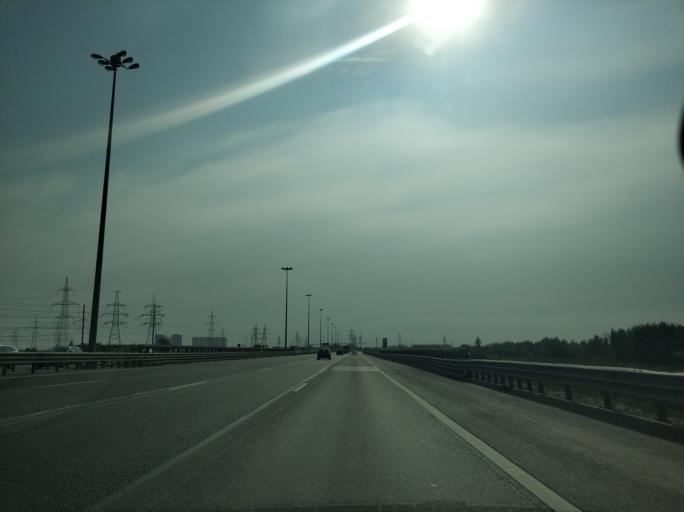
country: RU
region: Leningrad
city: Murino
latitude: 60.0254
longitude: 30.4497
